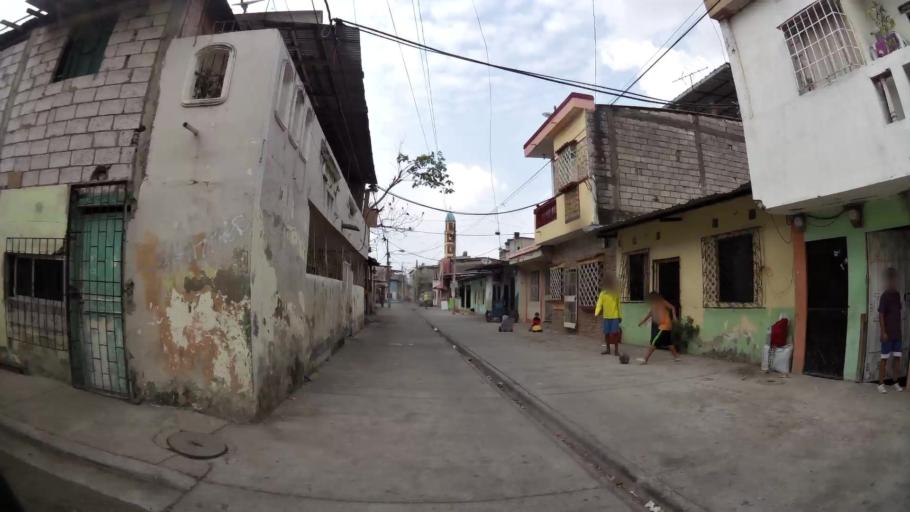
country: EC
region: Guayas
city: Guayaquil
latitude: -2.2347
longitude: -79.9073
